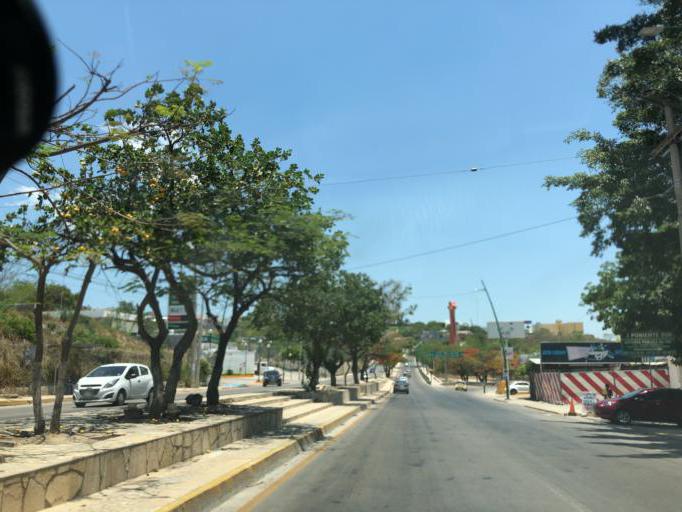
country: MX
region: Chiapas
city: Tuxtla Gutierrez
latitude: 16.7459
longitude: -93.1380
